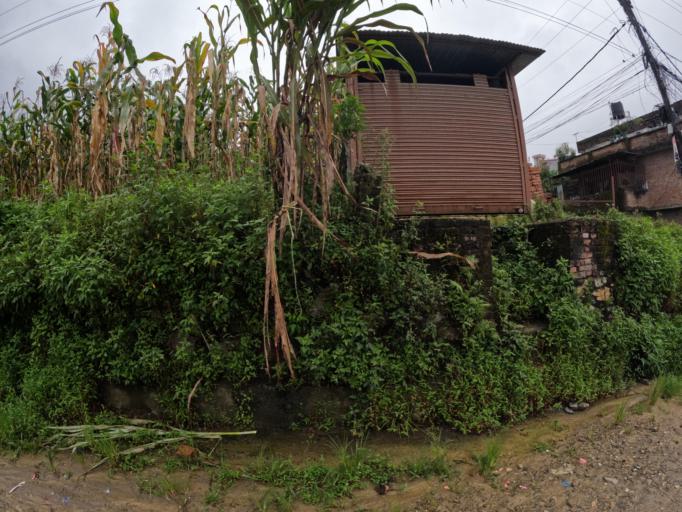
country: NP
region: Central Region
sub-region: Bagmati Zone
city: Kathmandu
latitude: 27.7598
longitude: 85.3188
